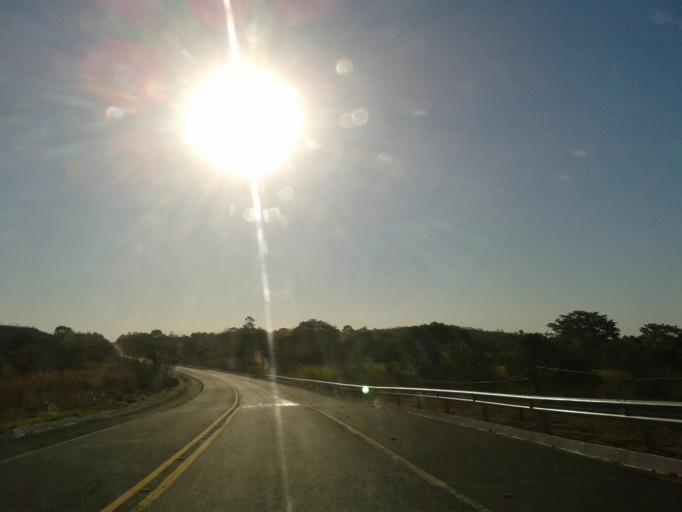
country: BR
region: Minas Gerais
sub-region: Santa Vitoria
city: Santa Vitoria
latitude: -19.1725
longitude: -50.0485
